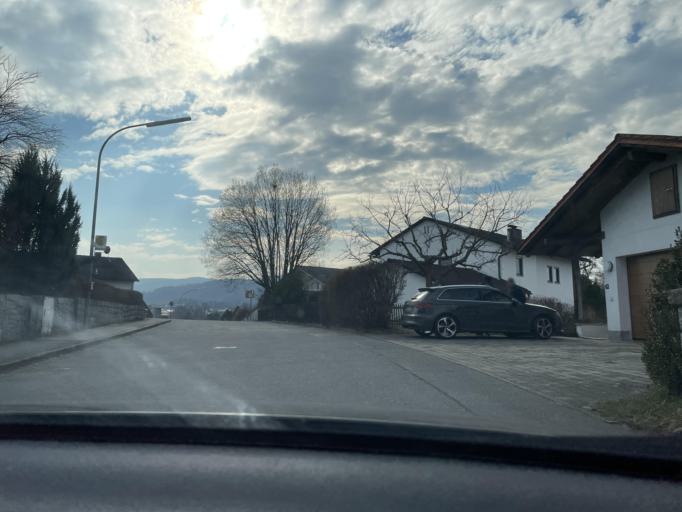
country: DE
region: Bavaria
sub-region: Lower Bavaria
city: Viechtach
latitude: 49.0879
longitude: 12.8872
